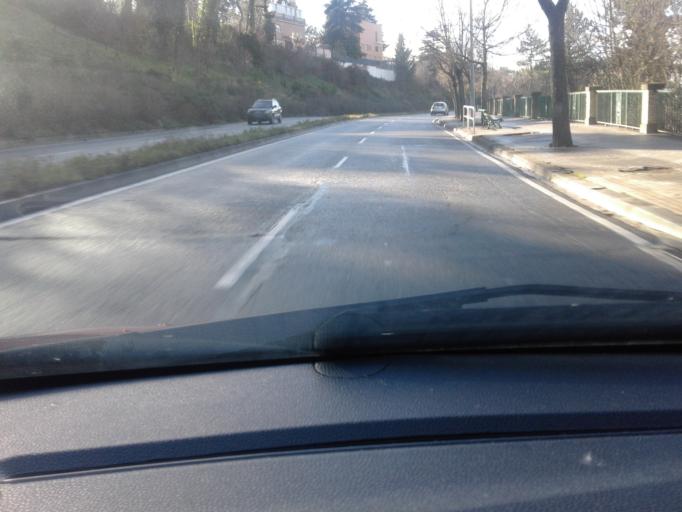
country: ES
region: Navarre
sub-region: Provincia de Navarra
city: Burlata
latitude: 42.8166
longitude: -1.6249
